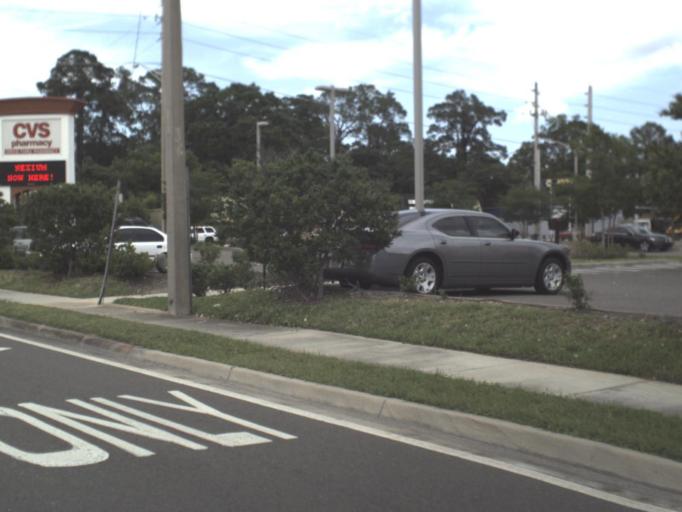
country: US
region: Florida
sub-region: Clay County
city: Bellair-Meadowbrook Terrace
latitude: 30.2478
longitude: -81.7430
